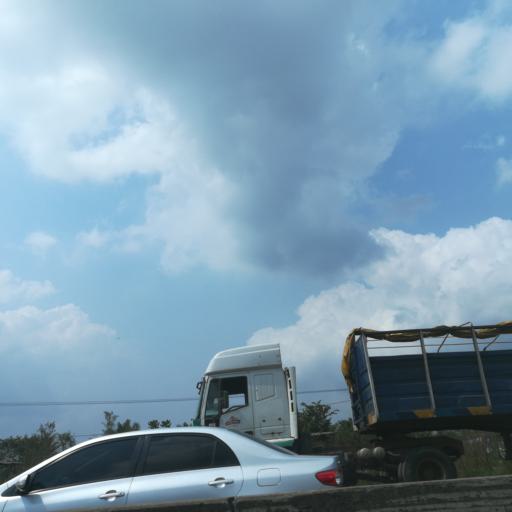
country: NG
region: Rivers
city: Okrika
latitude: 4.8123
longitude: 7.0977
